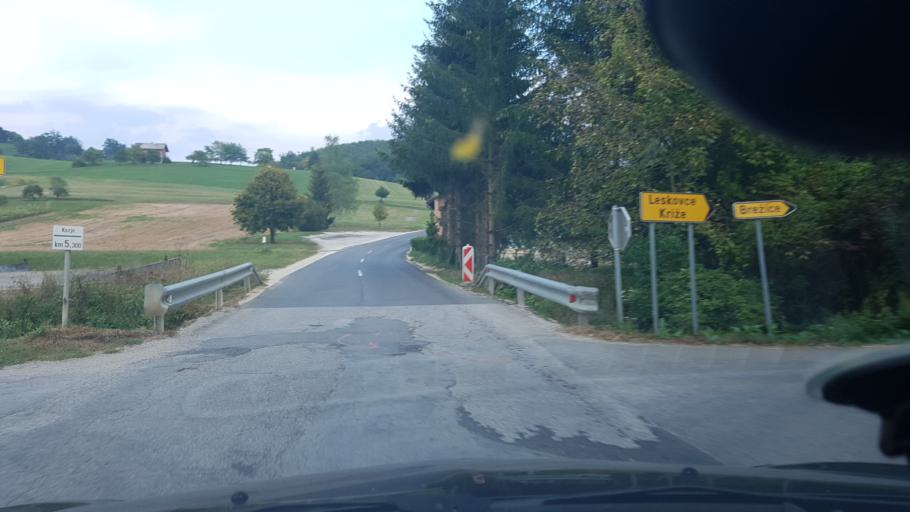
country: SI
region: Kozje
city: Kozje
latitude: 46.0346
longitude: 15.5415
